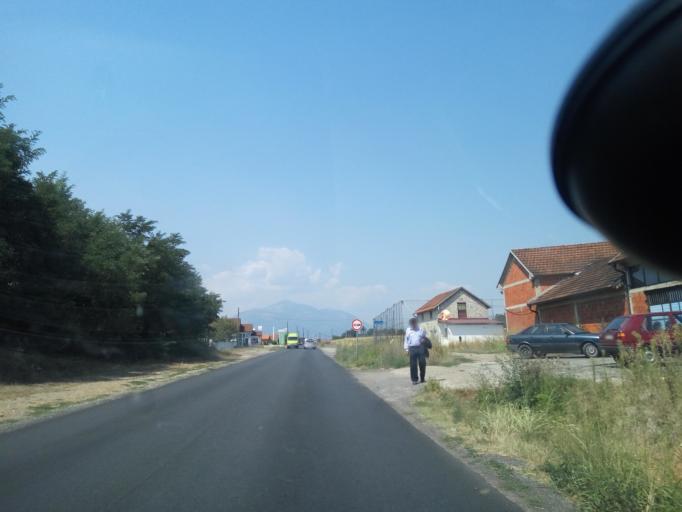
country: XK
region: Gjakova
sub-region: Komuna e Decanit
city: Gllogjan
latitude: 42.4426
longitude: 20.3663
